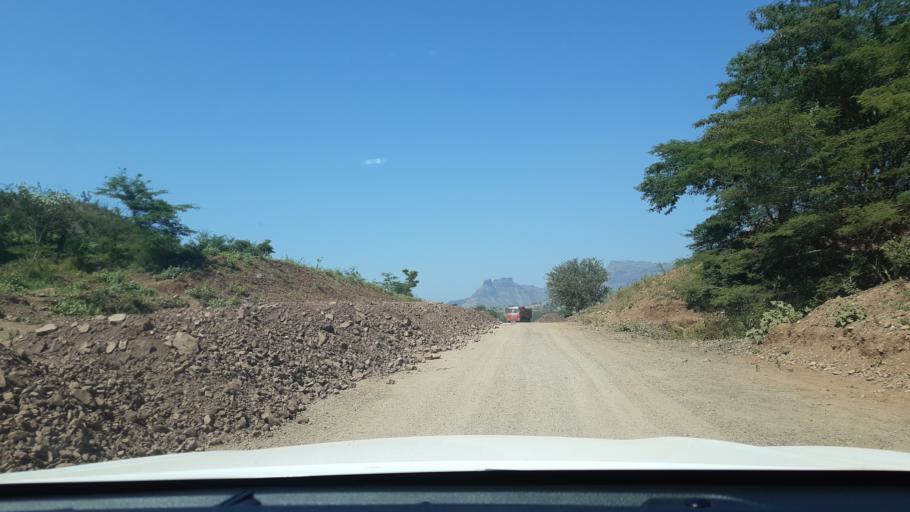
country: ET
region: Amhara
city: Dabat
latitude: 13.1931
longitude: 37.5697
